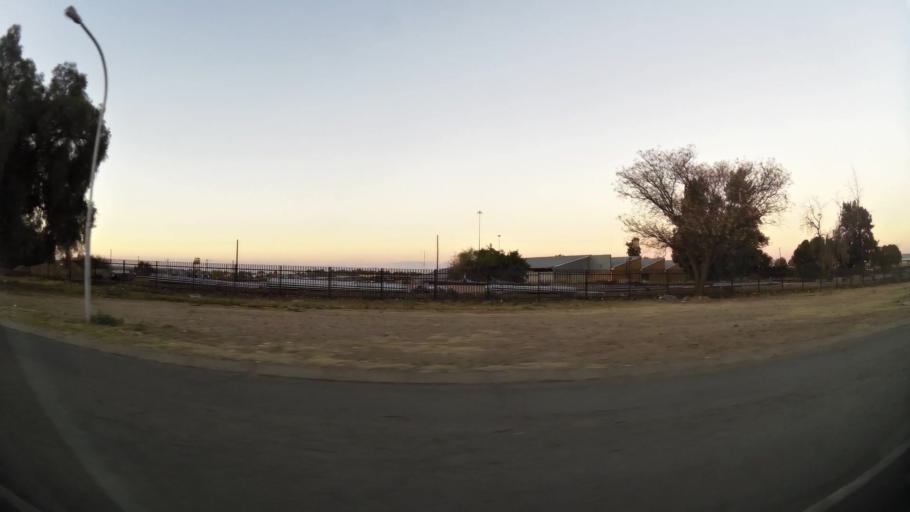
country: ZA
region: Northern Cape
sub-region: Frances Baard District Municipality
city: Kimberley
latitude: -28.7158
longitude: 24.7720
